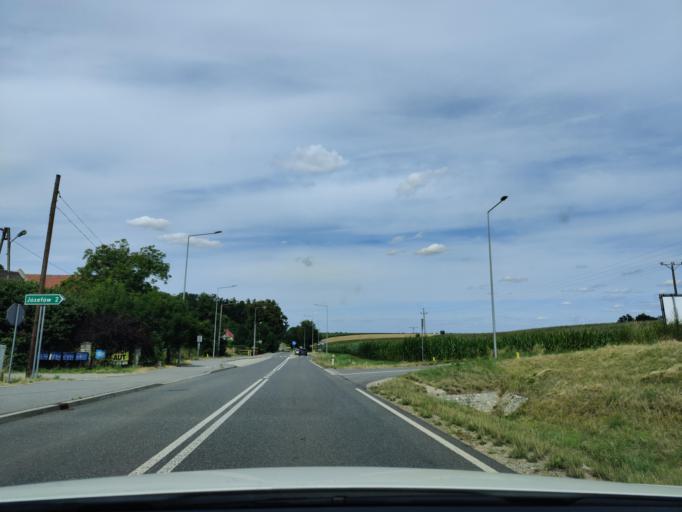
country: PL
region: Opole Voivodeship
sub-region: Powiat prudnicki
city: Lubrza
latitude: 50.3582
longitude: 17.6426
